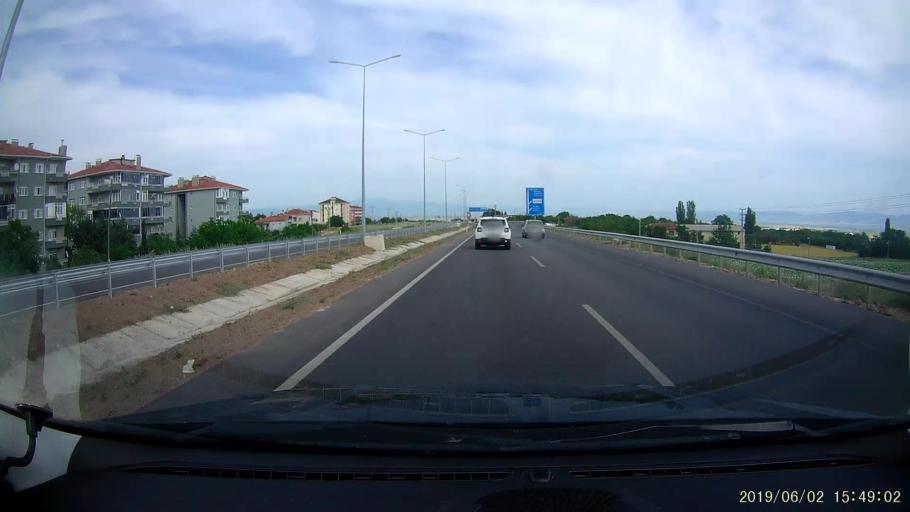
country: TR
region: Amasya
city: Merzifon
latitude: 40.8592
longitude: 35.4535
